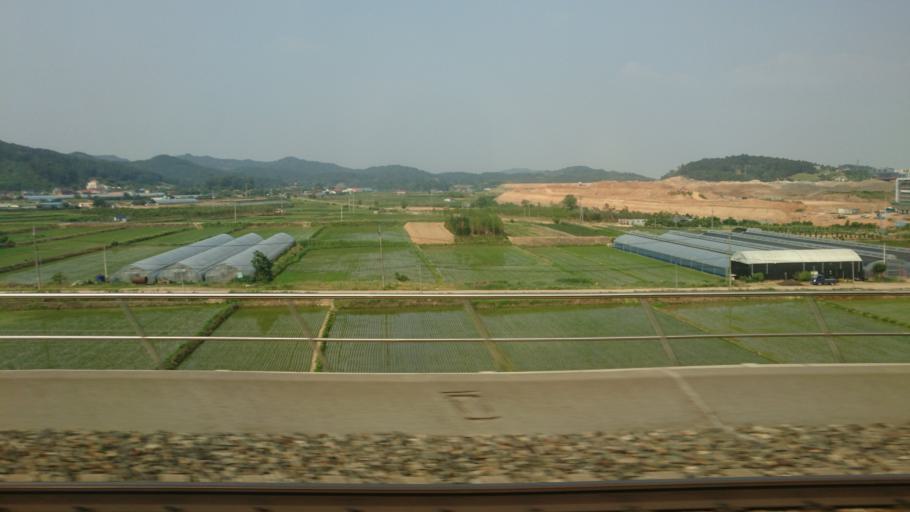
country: KR
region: Chungcheongbuk-do
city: Cheongju-si
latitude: 36.6371
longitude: 127.3085
